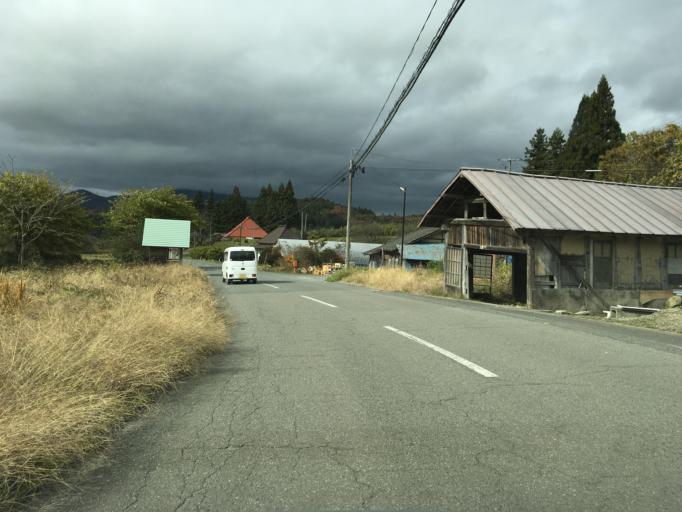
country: JP
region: Iwate
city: Mizusawa
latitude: 39.0640
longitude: 141.3868
